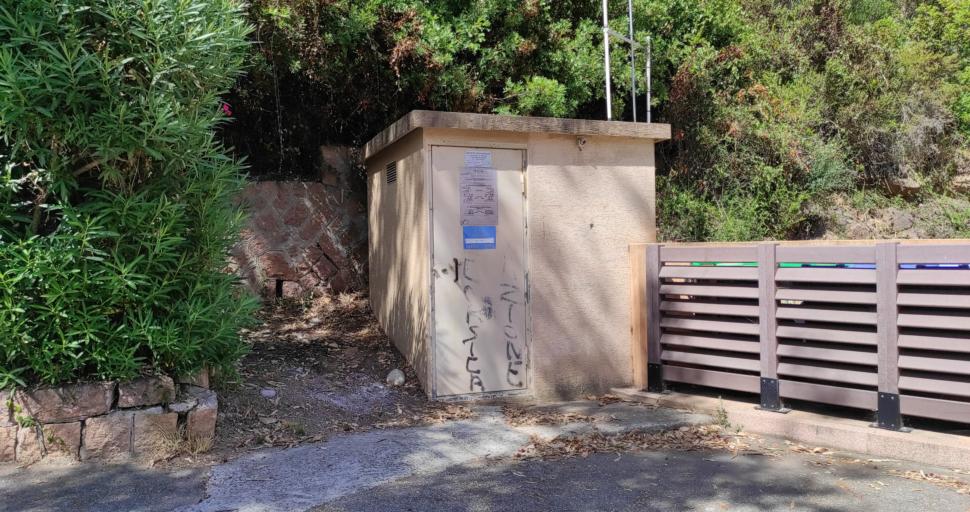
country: FR
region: Corsica
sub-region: Departement de la Corse-du-Sud
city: Cargese
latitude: 42.2674
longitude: 8.6962
